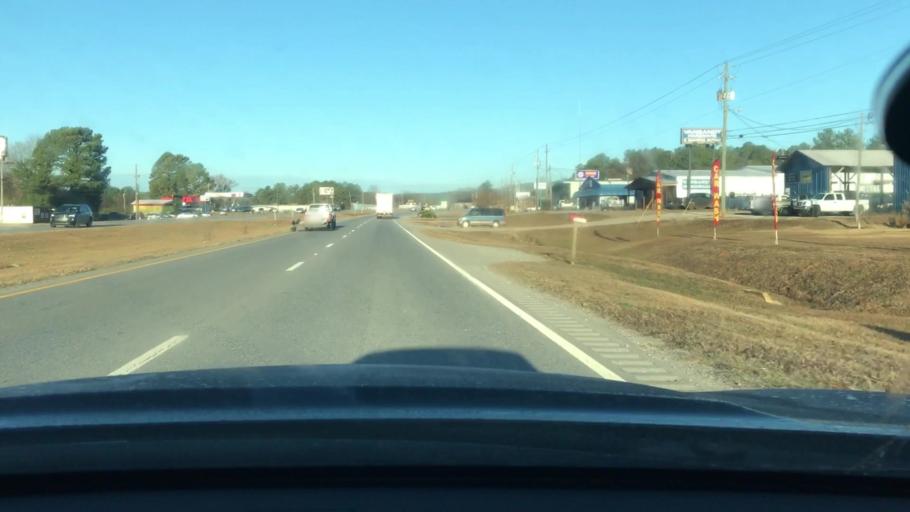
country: US
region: Alabama
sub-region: Talladega County
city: Mignon
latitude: 33.1779
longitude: -86.2945
